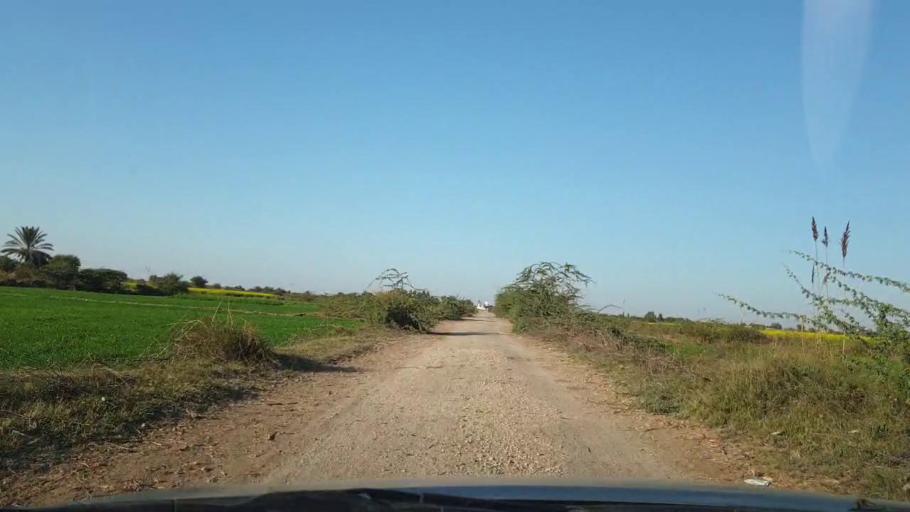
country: PK
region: Sindh
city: Jhol
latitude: 25.9040
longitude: 68.9251
